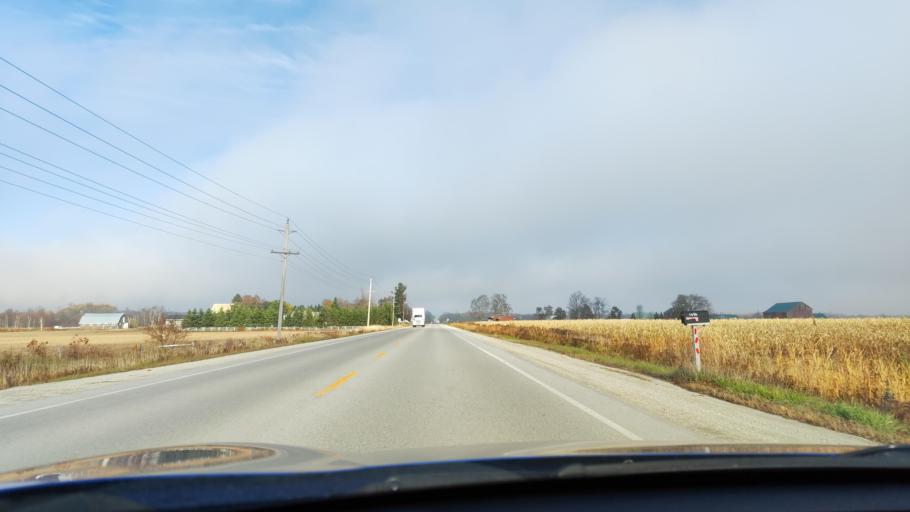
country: CA
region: Ontario
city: Wasaga Beach
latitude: 44.4525
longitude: -80.0706
